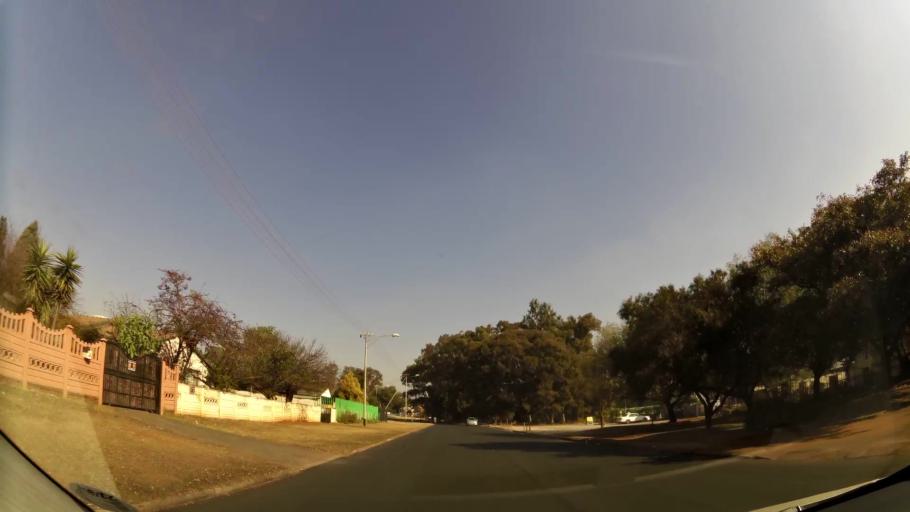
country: ZA
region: Gauteng
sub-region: West Rand District Municipality
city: Randfontein
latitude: -26.1650
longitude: 27.6895
